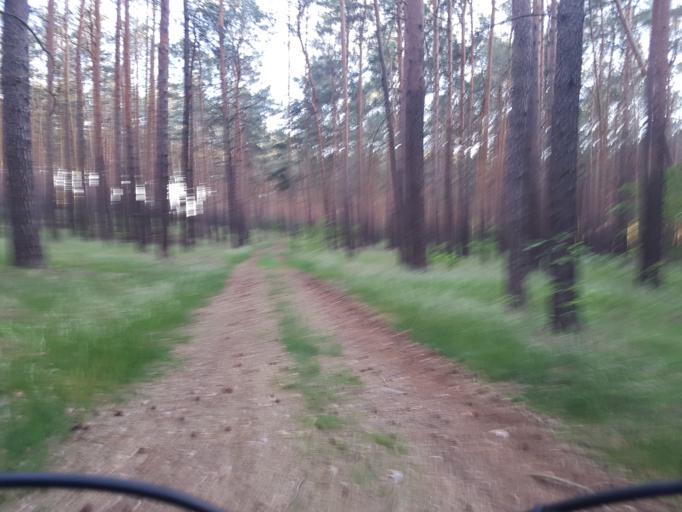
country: DE
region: Brandenburg
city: Schilda
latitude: 51.5618
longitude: 13.3805
